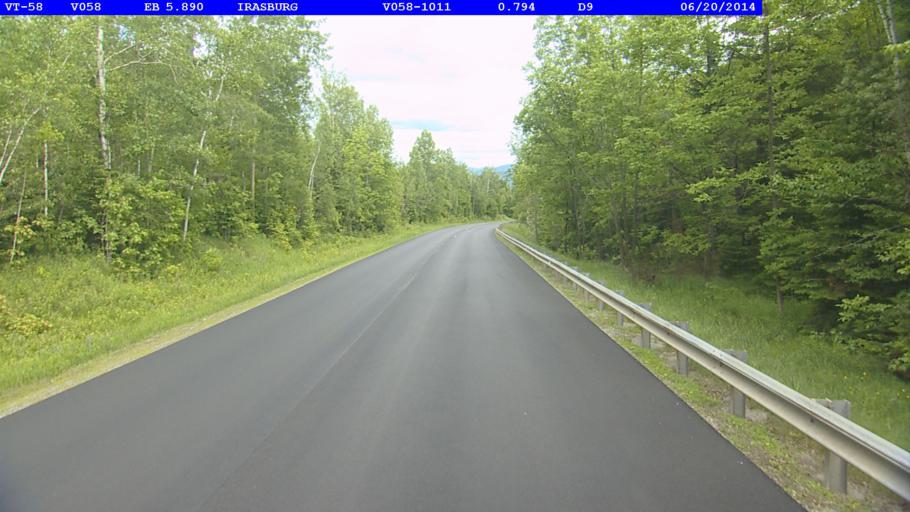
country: US
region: Vermont
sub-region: Orleans County
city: Newport
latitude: 44.8188
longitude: -72.3431
